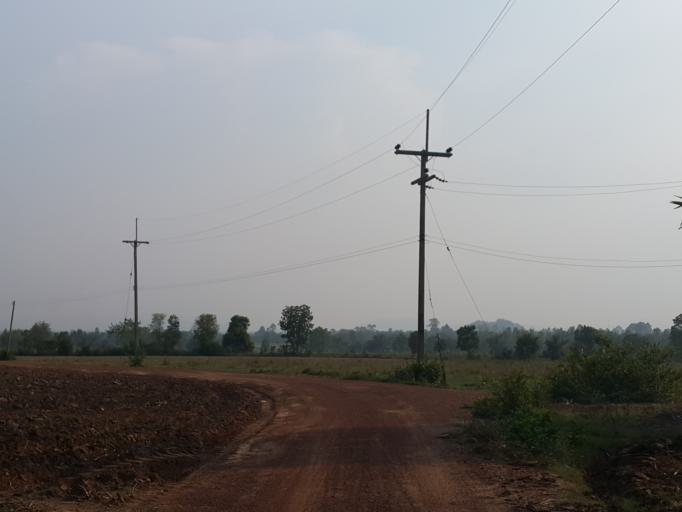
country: TH
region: Uthai Thani
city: Huai Khot
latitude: 15.3254
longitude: 99.6774
